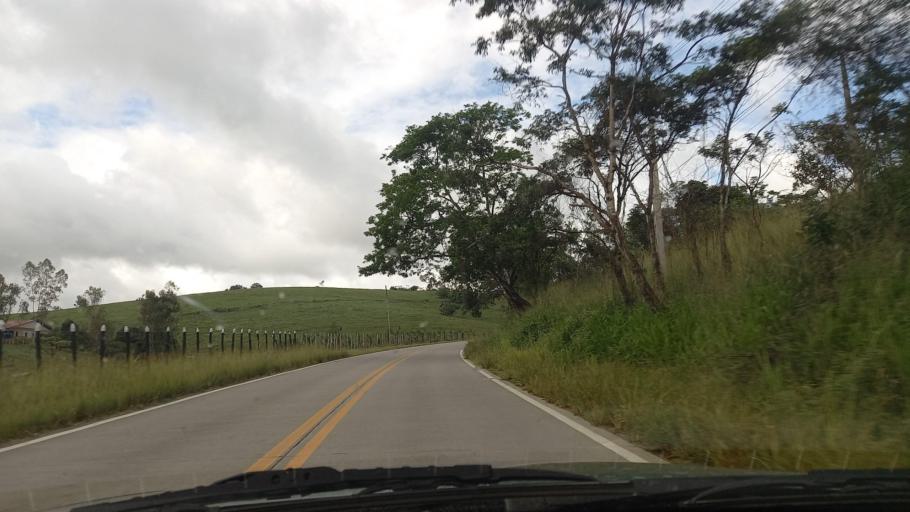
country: BR
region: Pernambuco
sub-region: Quipapa
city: Quipapa
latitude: -8.7877
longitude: -35.9706
